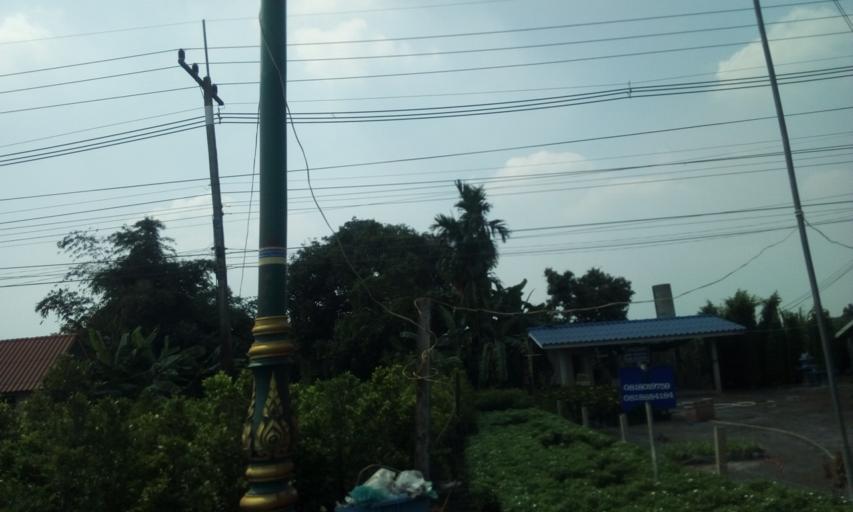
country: TH
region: Nakhon Nayok
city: Ongkharak
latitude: 14.1231
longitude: 100.9430
